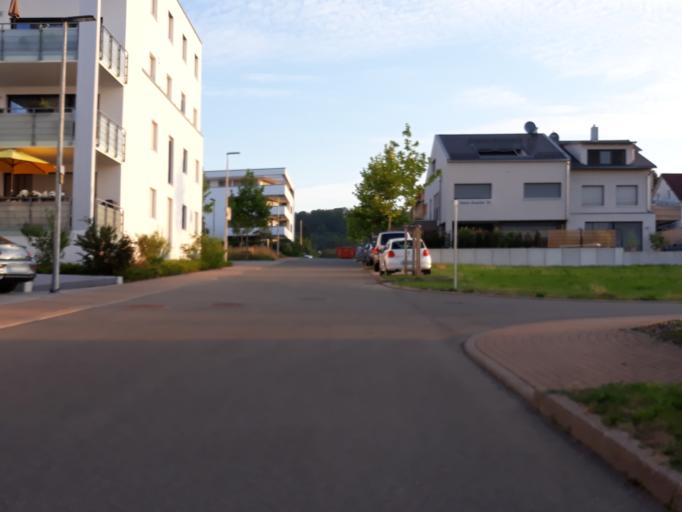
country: DE
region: Baden-Wuerttemberg
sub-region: Regierungsbezirk Stuttgart
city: Schonaich
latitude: 48.6605
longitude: 9.0542
